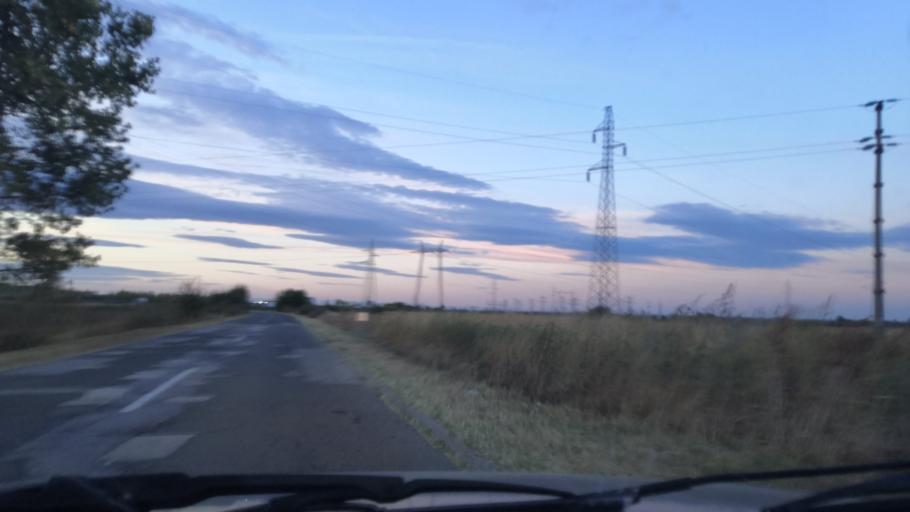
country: RS
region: Central Serbia
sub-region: Borski Okrug
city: Negotin
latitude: 44.2887
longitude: 22.5574
